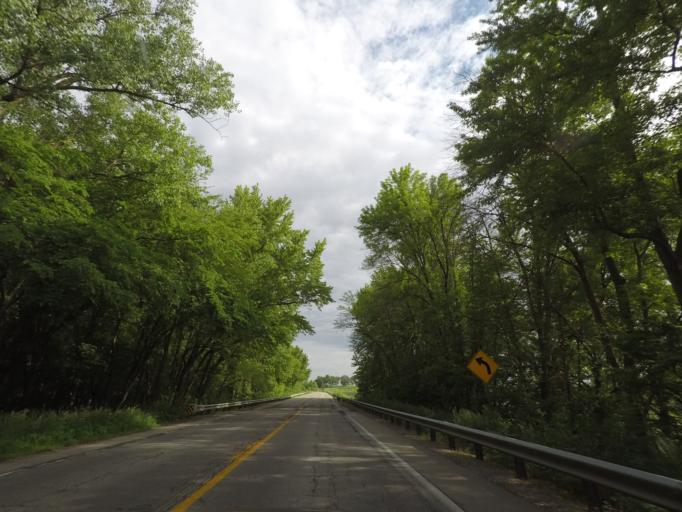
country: US
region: Illinois
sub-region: Logan County
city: Mount Pulaski
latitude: 40.0560
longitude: -89.2820
